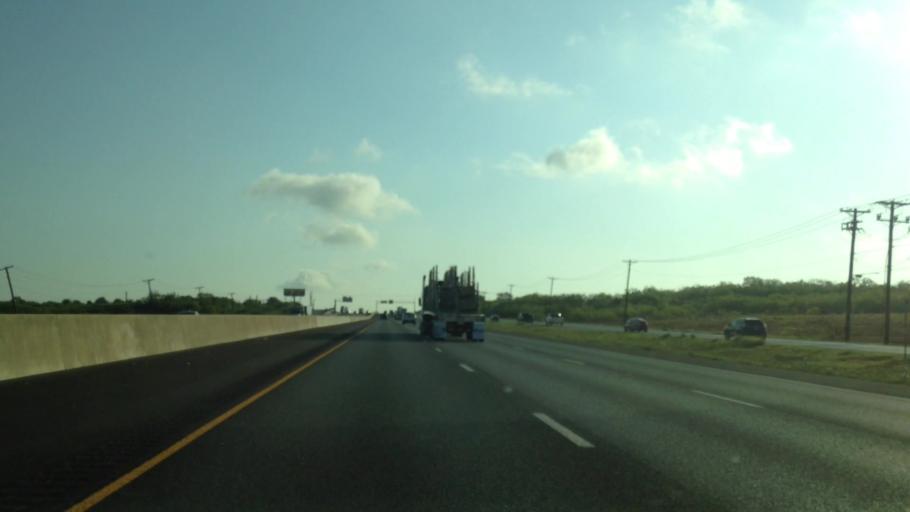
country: US
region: Texas
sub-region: Guadalupe County
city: Lake Dunlap
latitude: 29.7393
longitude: -98.0653
